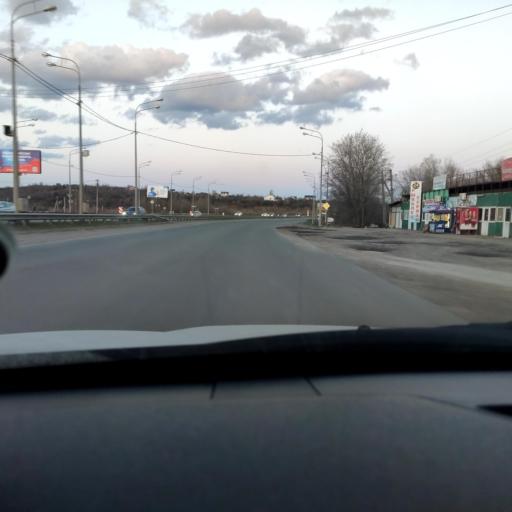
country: RU
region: Samara
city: Smyshlyayevka
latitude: 53.2665
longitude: 50.4013
